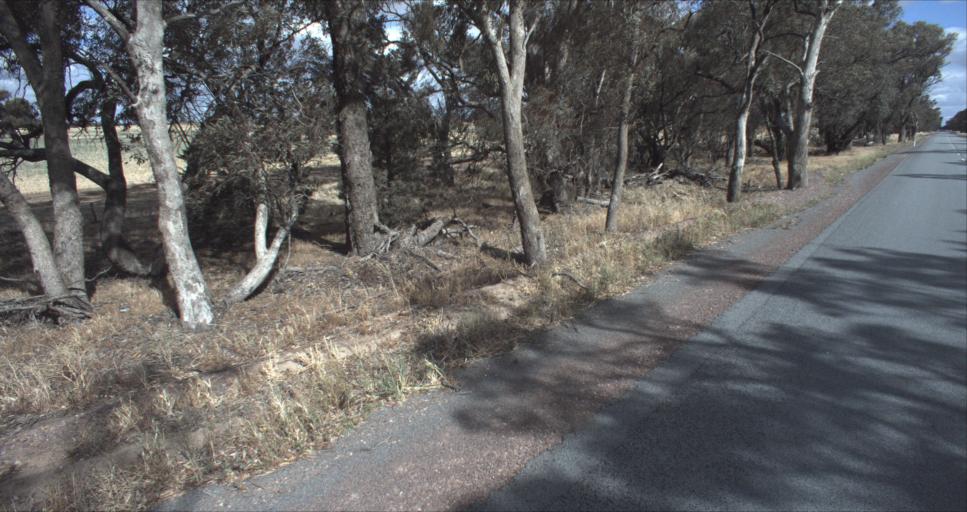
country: AU
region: New South Wales
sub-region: Leeton
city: Leeton
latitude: -34.6771
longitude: 146.3463
